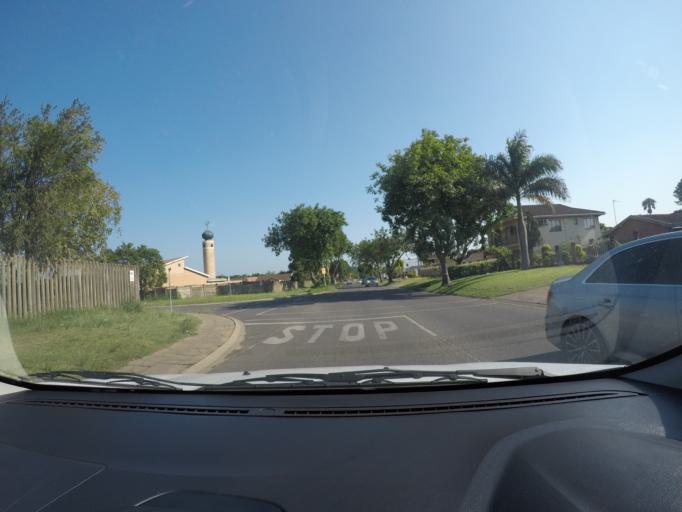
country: ZA
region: KwaZulu-Natal
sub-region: uThungulu District Municipality
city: Richards Bay
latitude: -28.7241
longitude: 32.0415
